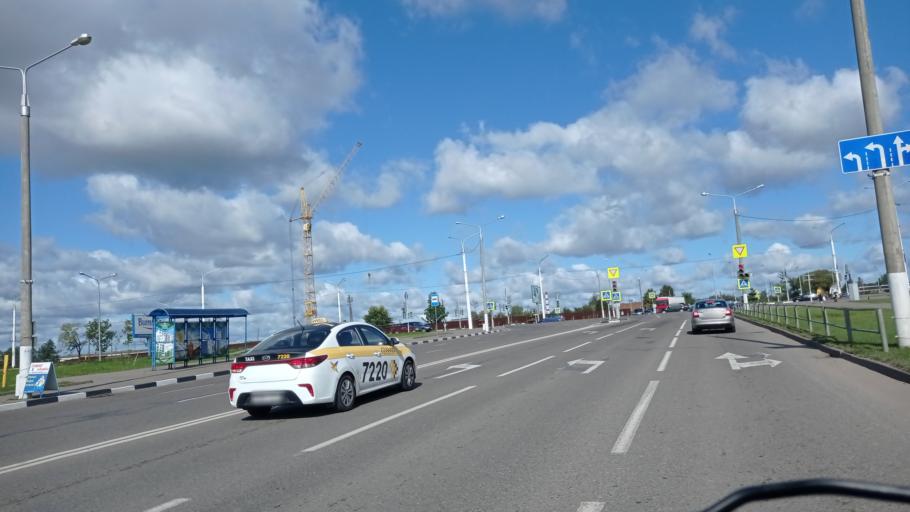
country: BY
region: Vitebsk
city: Vitebsk
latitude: 55.1732
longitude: 30.2585
